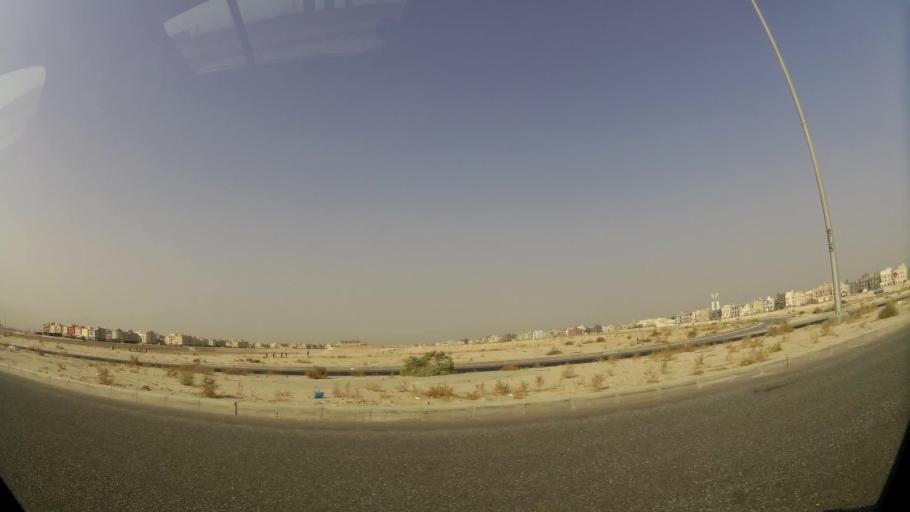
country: KW
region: Muhafazat al Jahra'
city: Al Jahra'
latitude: 29.3441
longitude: 47.7807
